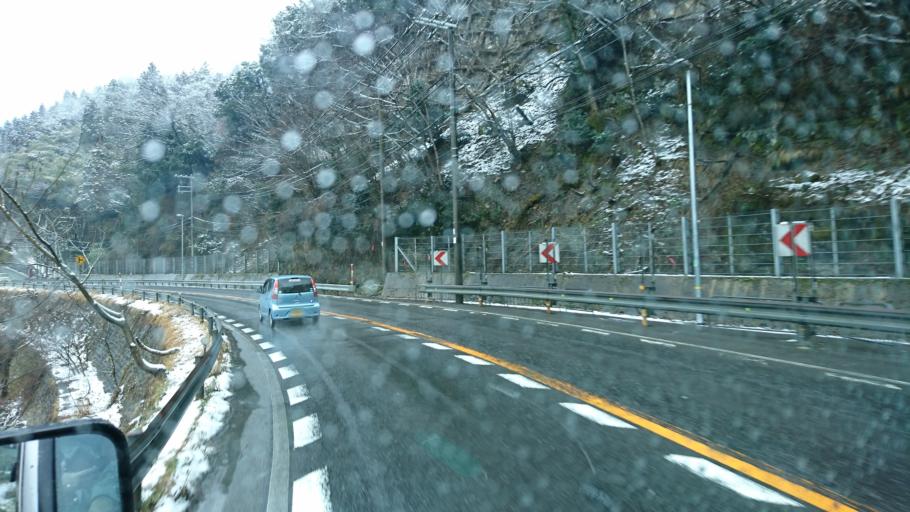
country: JP
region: Hyogo
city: Toyooka
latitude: 35.4803
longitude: 134.5863
